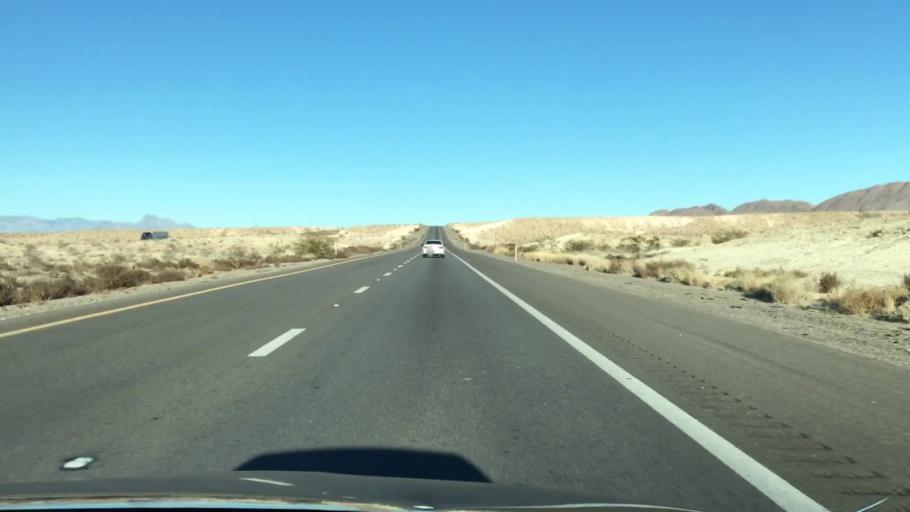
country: US
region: Nevada
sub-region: Clark County
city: Moapa Town
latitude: 36.5650
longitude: -114.6777
